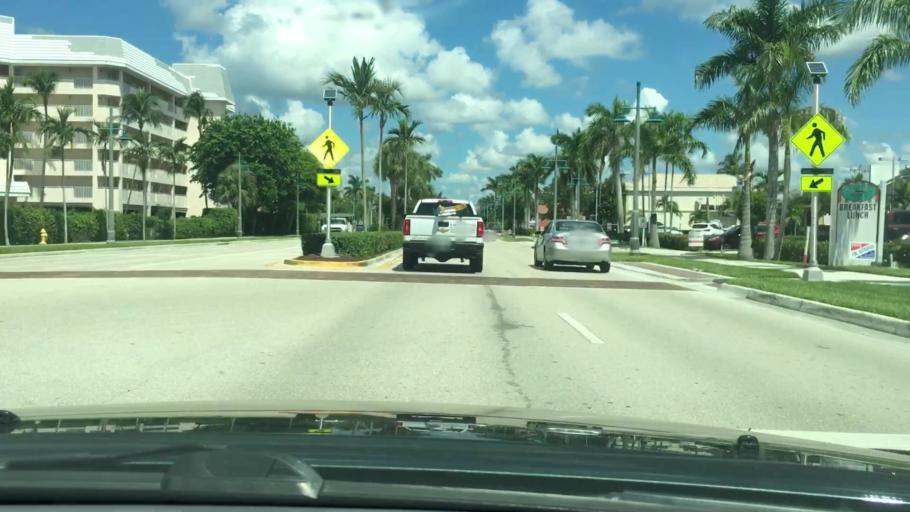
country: US
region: Florida
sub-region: Collier County
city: Marco
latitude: 25.9435
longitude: -81.7325
